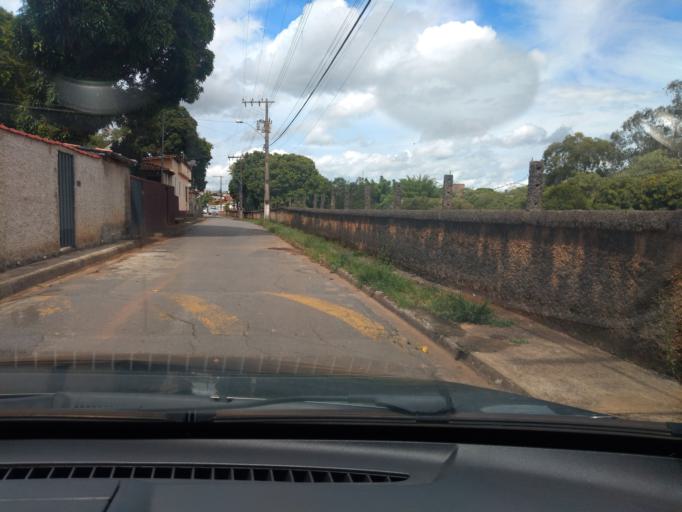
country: BR
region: Minas Gerais
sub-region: Tres Coracoes
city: Tres Coracoes
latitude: -21.6989
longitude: -45.2670
